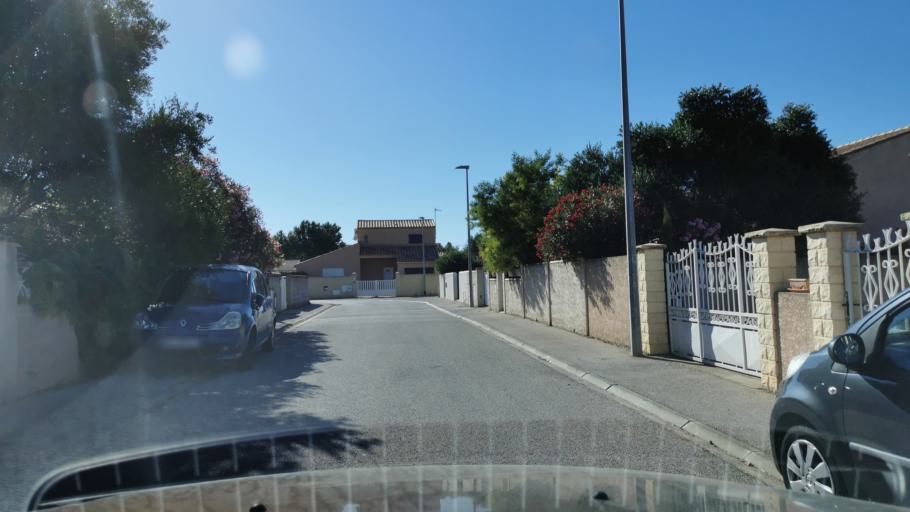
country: FR
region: Languedoc-Roussillon
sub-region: Departement de l'Aude
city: Narbonne
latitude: 43.1976
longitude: 3.0207
